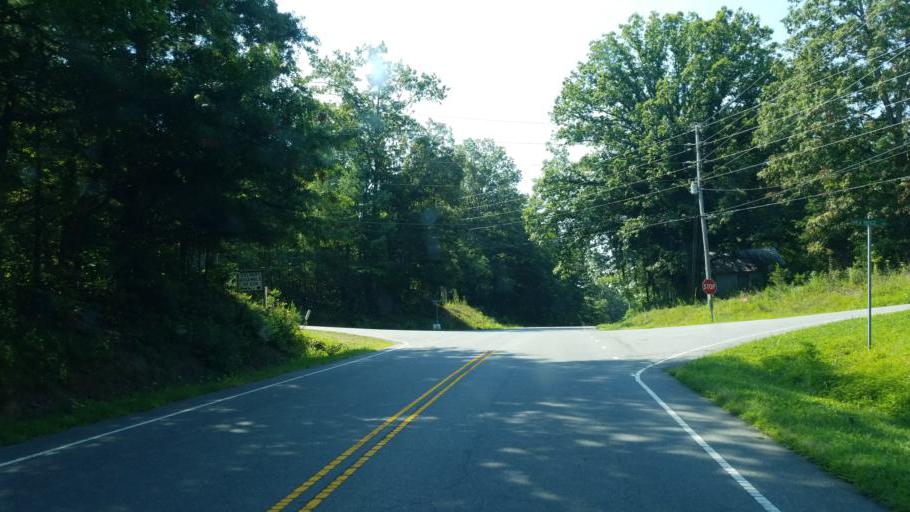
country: US
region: North Carolina
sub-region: Burke County
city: Glen Alpine
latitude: 35.8108
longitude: -81.7884
